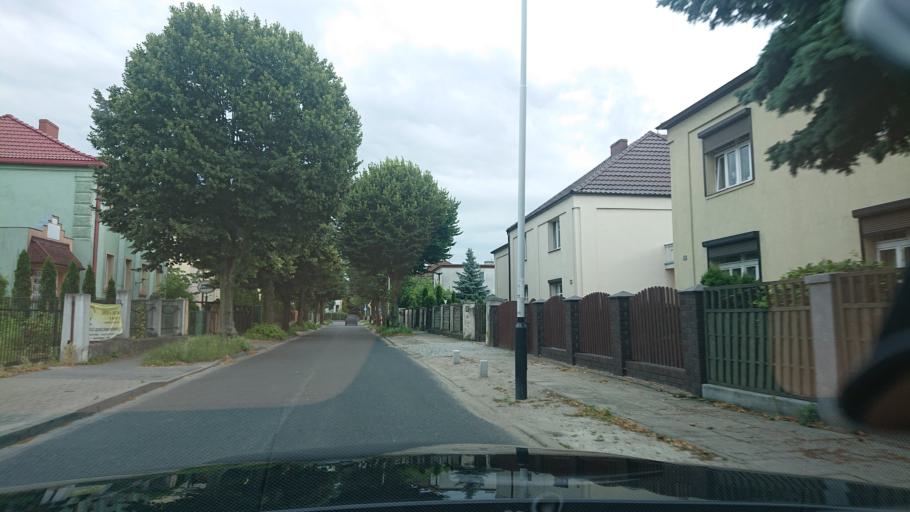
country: PL
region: Greater Poland Voivodeship
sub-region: Powiat gnieznienski
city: Gniezno
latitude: 52.5372
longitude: 17.6152
